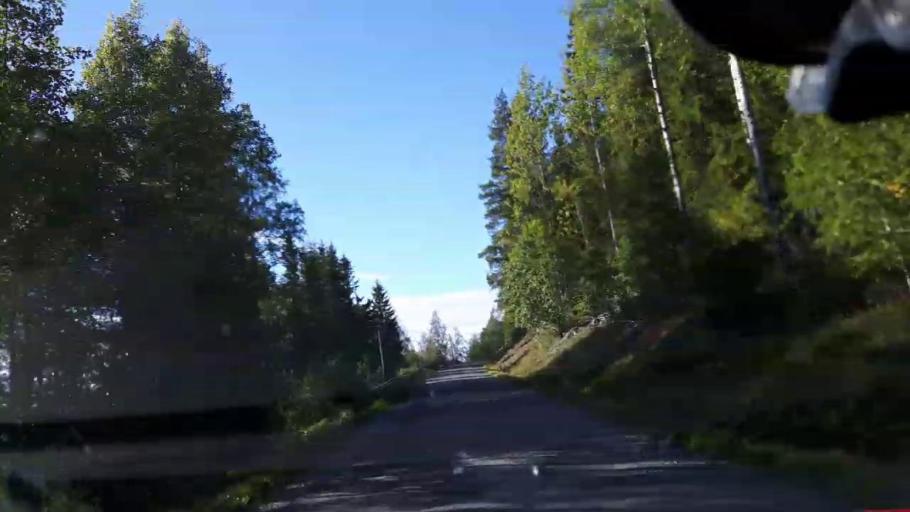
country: SE
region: Jaemtland
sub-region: Ragunda Kommun
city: Hammarstrand
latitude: 63.4933
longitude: 16.0409
